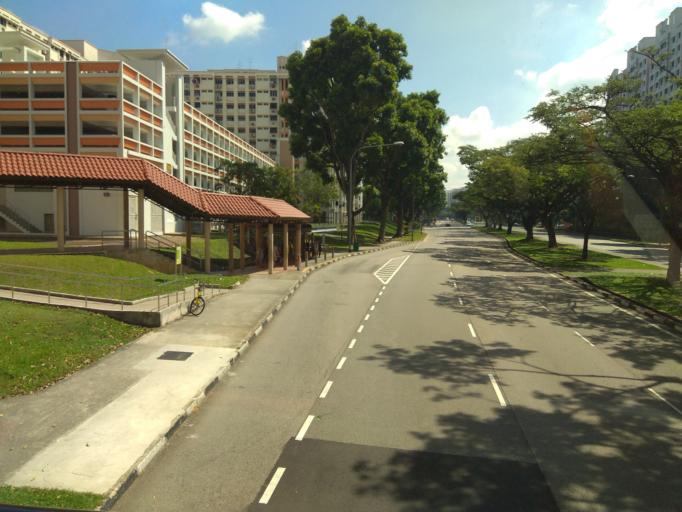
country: MY
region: Johor
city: Johor Bahru
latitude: 1.3450
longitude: 103.7005
